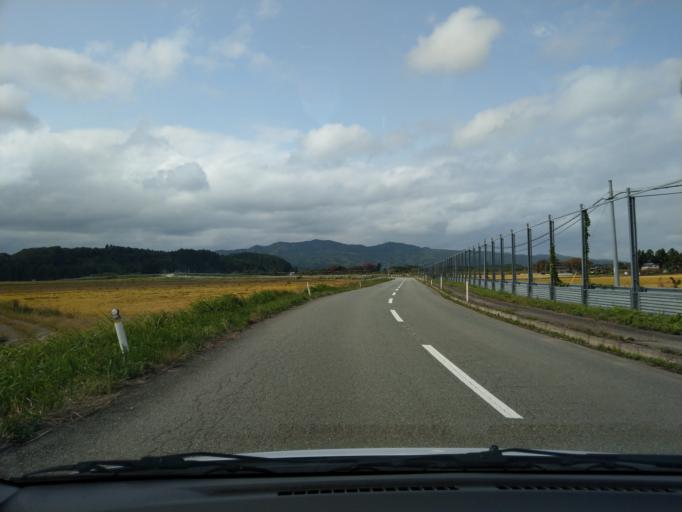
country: JP
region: Akita
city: Akita
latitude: 39.5289
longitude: 140.2572
